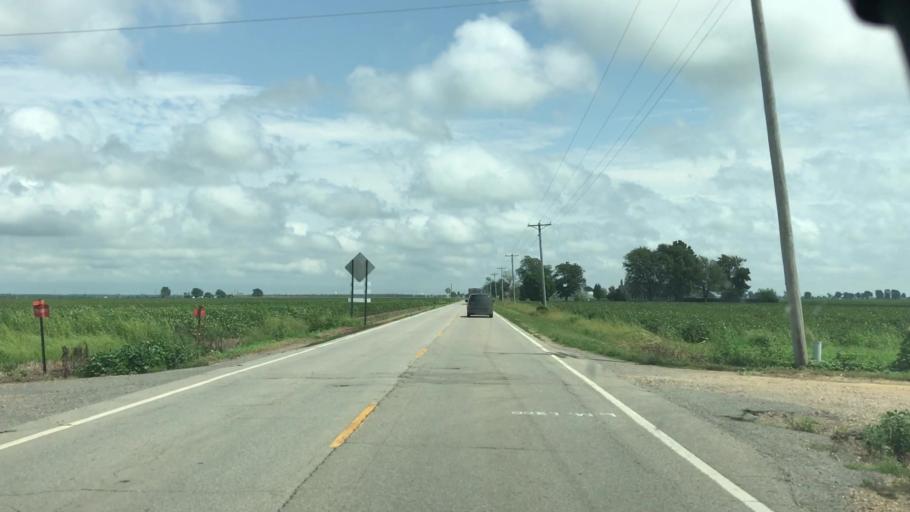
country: US
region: Missouri
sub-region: Pemiscot County
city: Hayti
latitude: 36.1759
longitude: -89.7358
